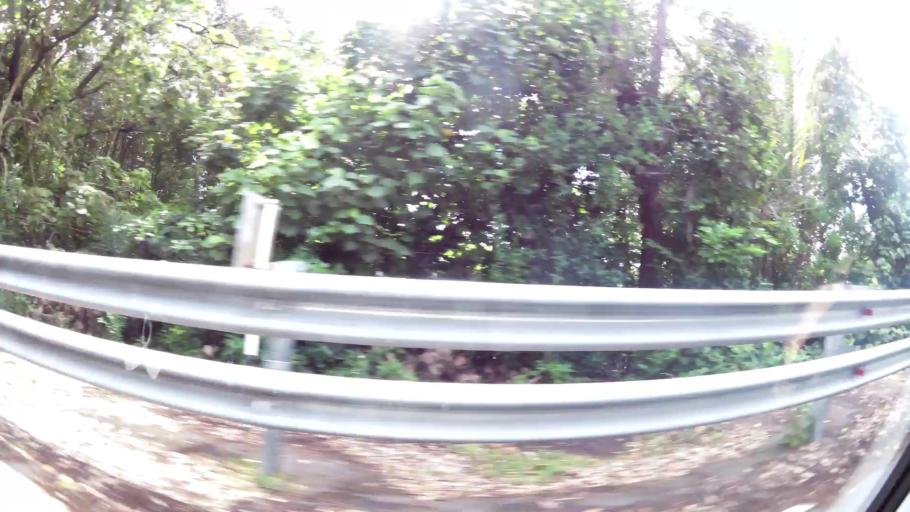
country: BN
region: Belait
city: Seria
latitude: 4.6067
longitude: 114.3003
